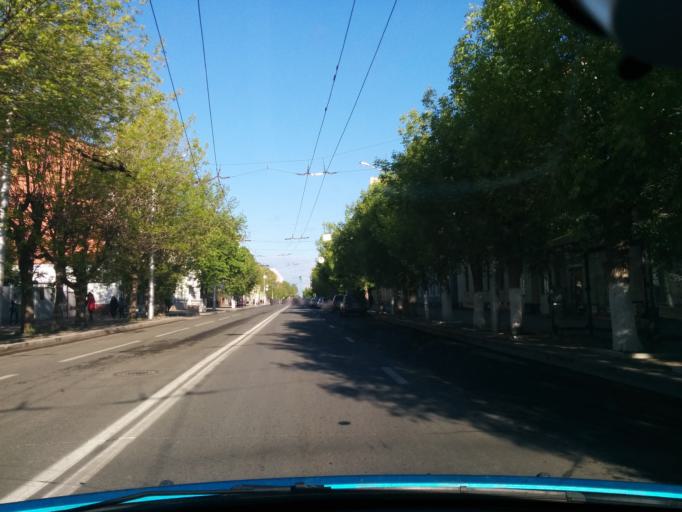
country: RU
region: Bashkortostan
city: Ufa
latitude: 54.7271
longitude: 55.9408
